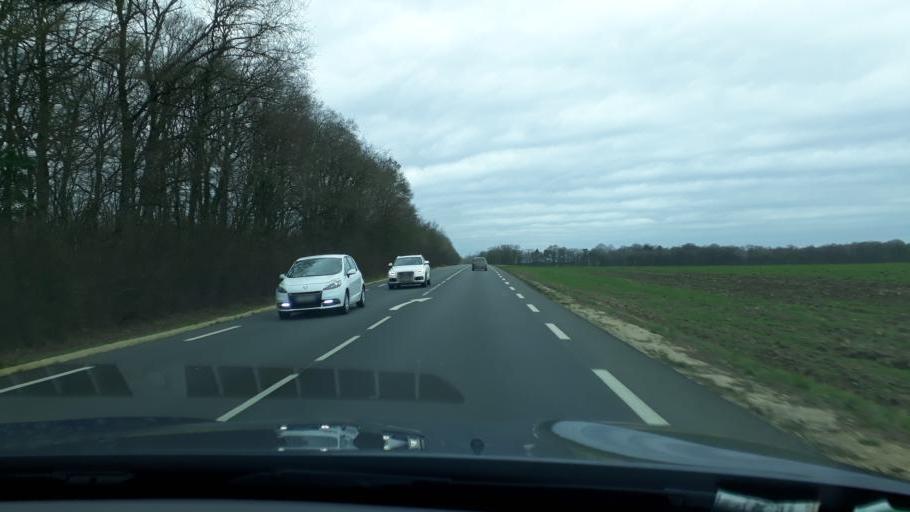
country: FR
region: Centre
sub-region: Departement du Loiret
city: Chanteau
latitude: 48.0189
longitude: 1.9630
